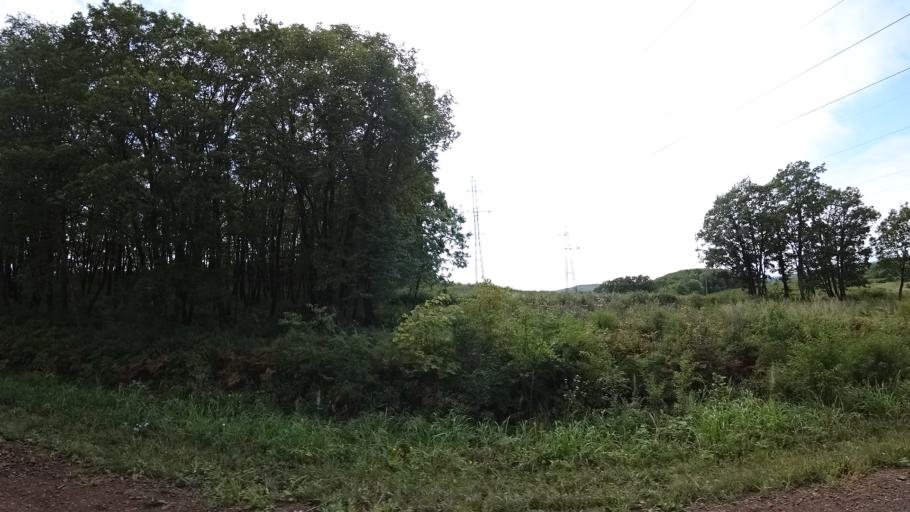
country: RU
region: Primorskiy
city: Lyalichi
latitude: 44.1426
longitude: 132.4043
